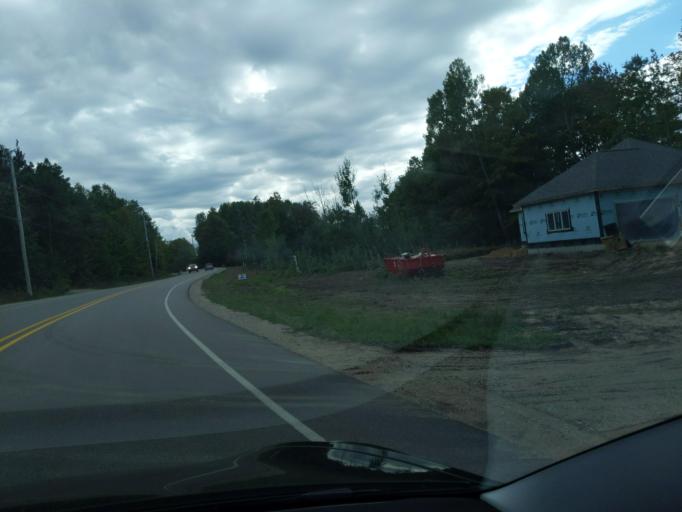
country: US
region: Michigan
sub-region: Kalkaska County
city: Rapid City
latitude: 44.9032
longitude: -85.2799
